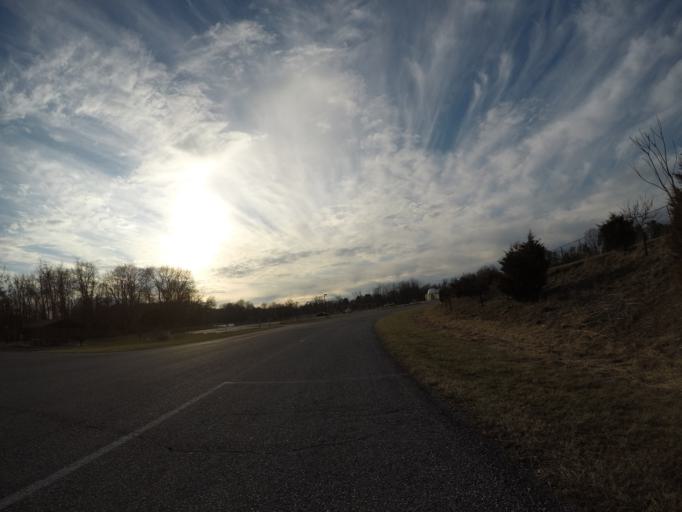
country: US
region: Maryland
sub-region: Carroll County
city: Sykesville
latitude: 39.3204
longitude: -76.9157
